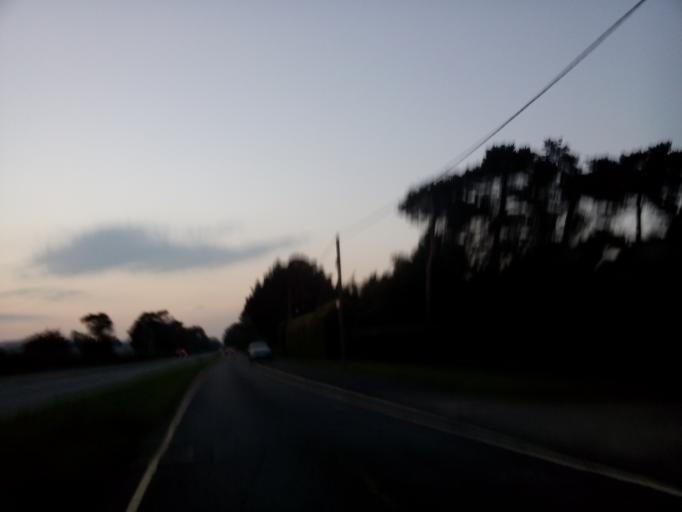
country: GB
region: England
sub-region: Suffolk
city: Kesgrave
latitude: 52.0288
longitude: 1.2269
